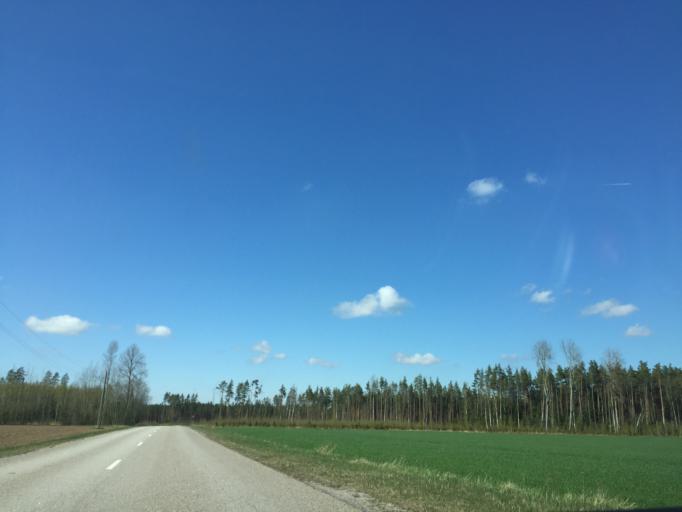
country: LV
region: Strenci
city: Seda
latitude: 57.5822
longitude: 25.7550
